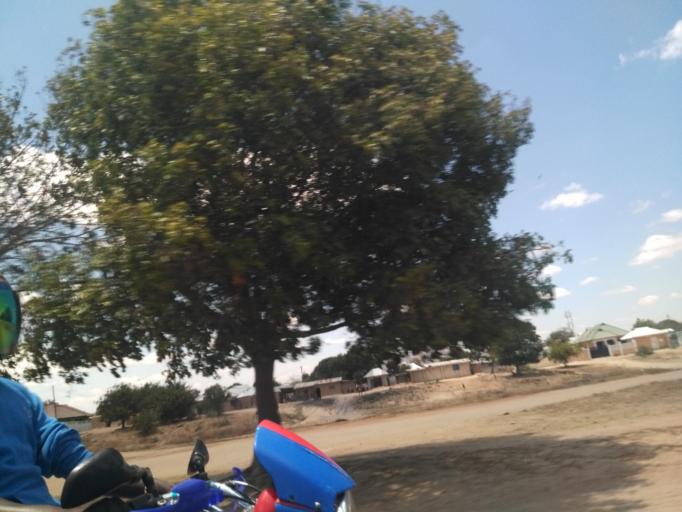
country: TZ
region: Dodoma
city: Kisasa
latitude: -6.1727
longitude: 35.7682
